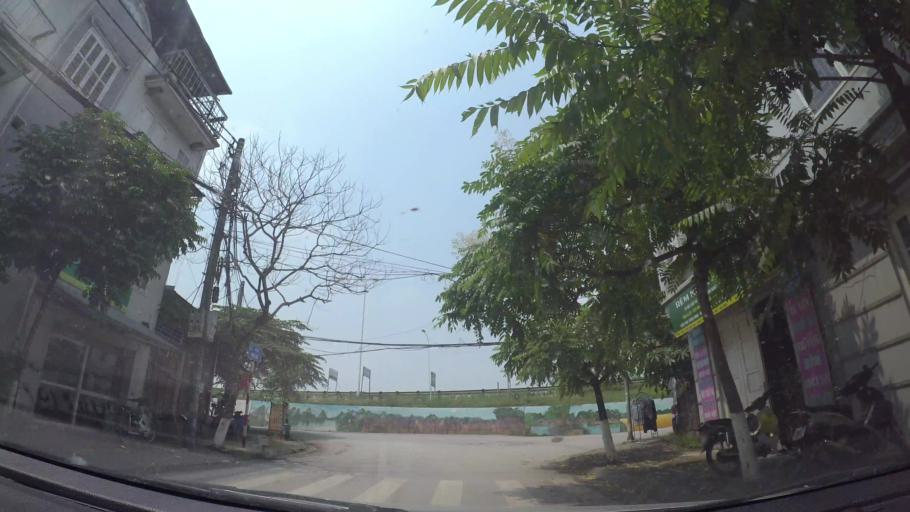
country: VN
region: Ha Noi
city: Tay Ho
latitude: 21.0895
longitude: 105.8085
